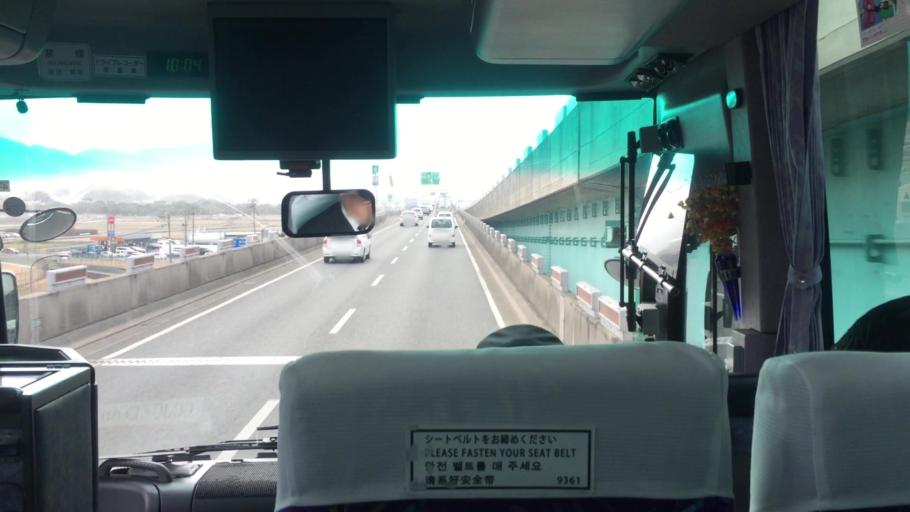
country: JP
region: Fukuoka
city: Onojo
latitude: 33.5723
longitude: 130.4547
